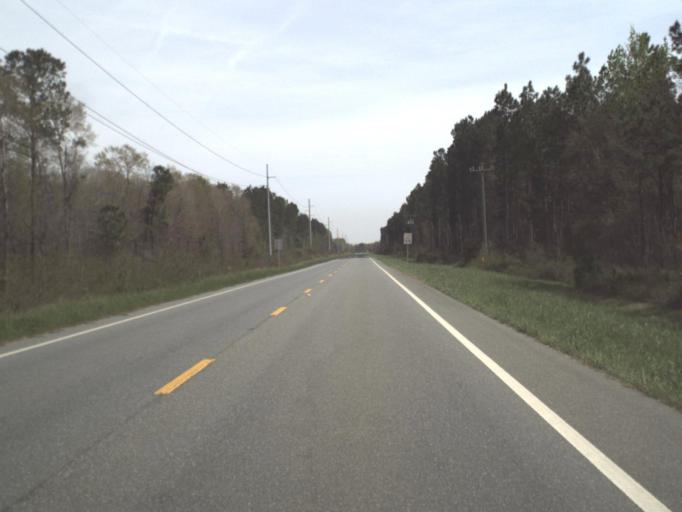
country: US
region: Alabama
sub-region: Houston County
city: Cottonwood
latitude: 30.9431
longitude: -85.3446
